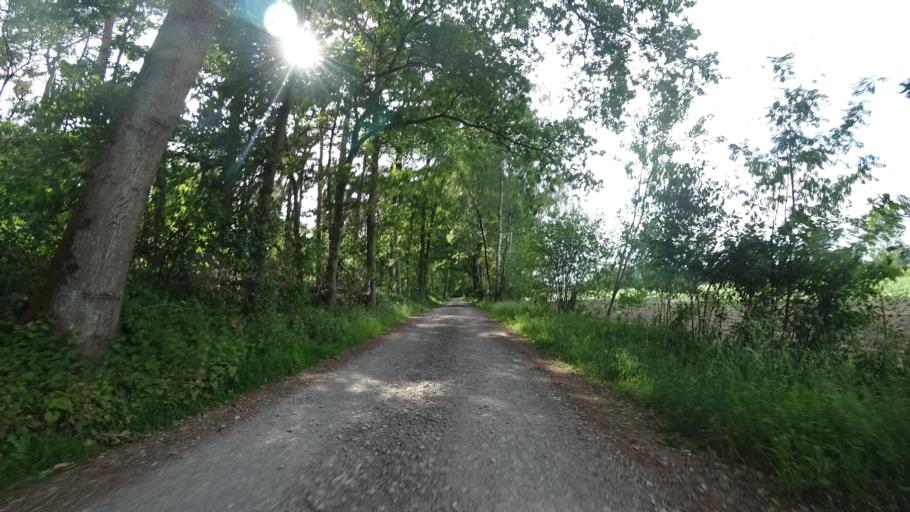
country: DE
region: North Rhine-Westphalia
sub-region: Regierungsbezirk Detmold
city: Verl
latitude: 51.9000
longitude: 8.4593
